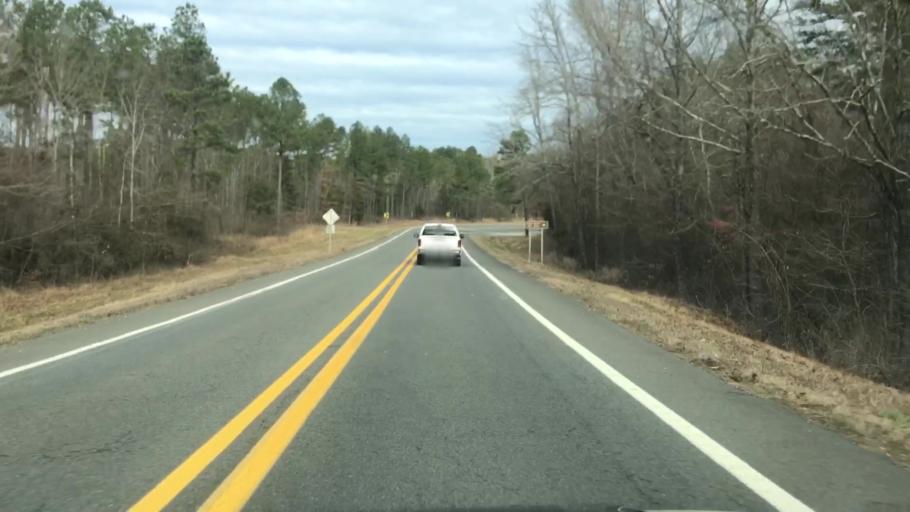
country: US
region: Arkansas
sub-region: Montgomery County
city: Mount Ida
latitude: 34.5917
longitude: -93.6652
